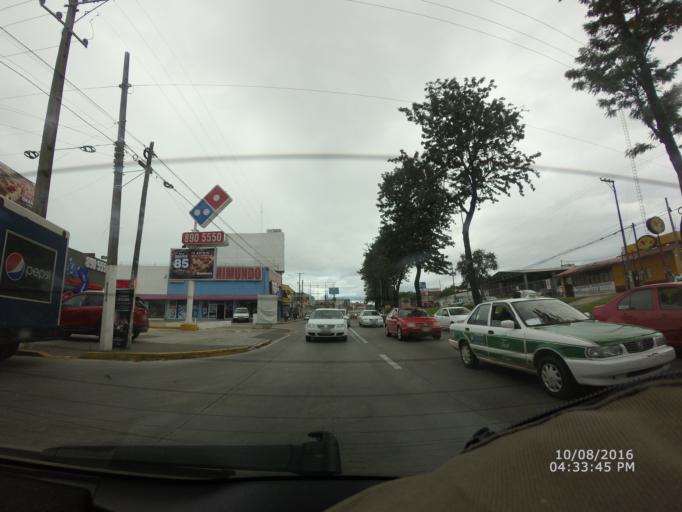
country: MX
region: Veracruz
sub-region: Xalapa
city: Xalapa de Enriquez
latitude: 19.5584
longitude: -96.9180
